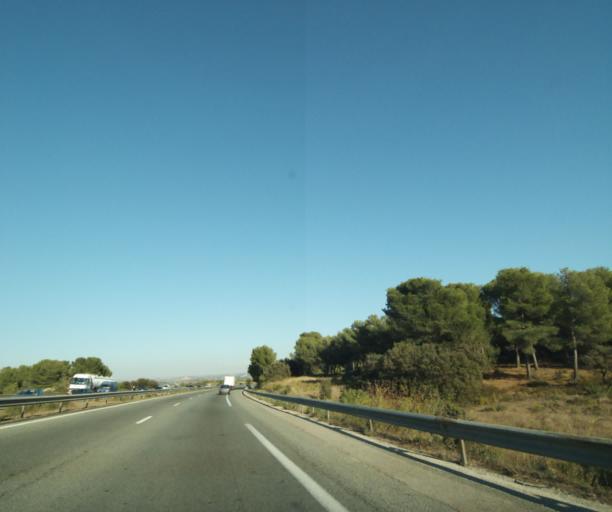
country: FR
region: Provence-Alpes-Cote d'Azur
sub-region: Departement des Bouches-du-Rhone
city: Ensues-la-Redonne
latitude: 43.3790
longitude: 5.2050
